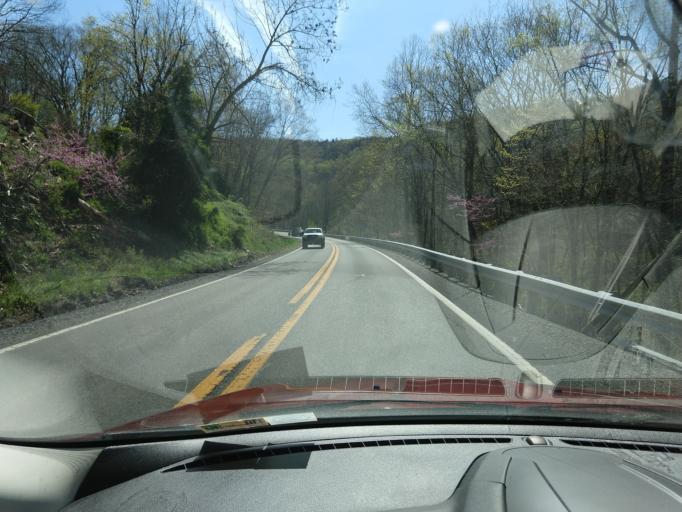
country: US
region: West Virginia
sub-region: Greenbrier County
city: Alderson
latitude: 37.7178
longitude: -80.6214
